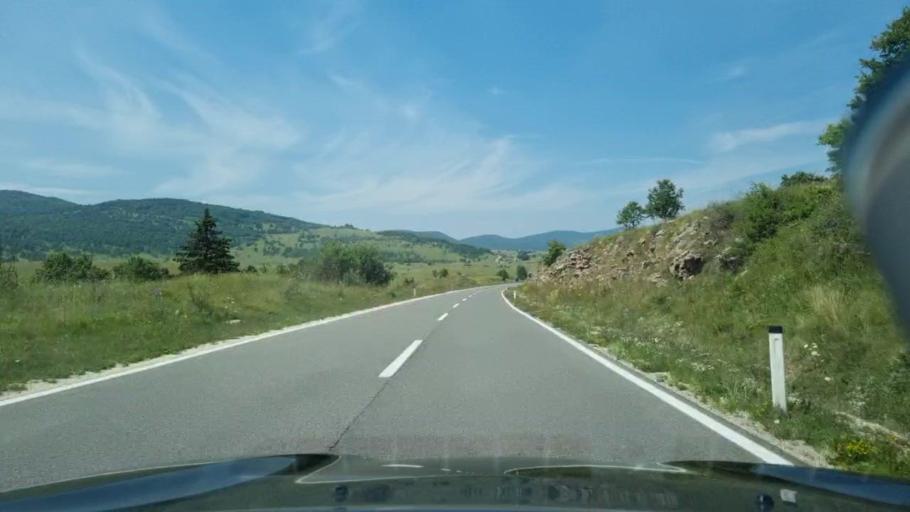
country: BA
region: Federation of Bosnia and Herzegovina
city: Sanica
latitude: 44.5580
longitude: 16.5049
